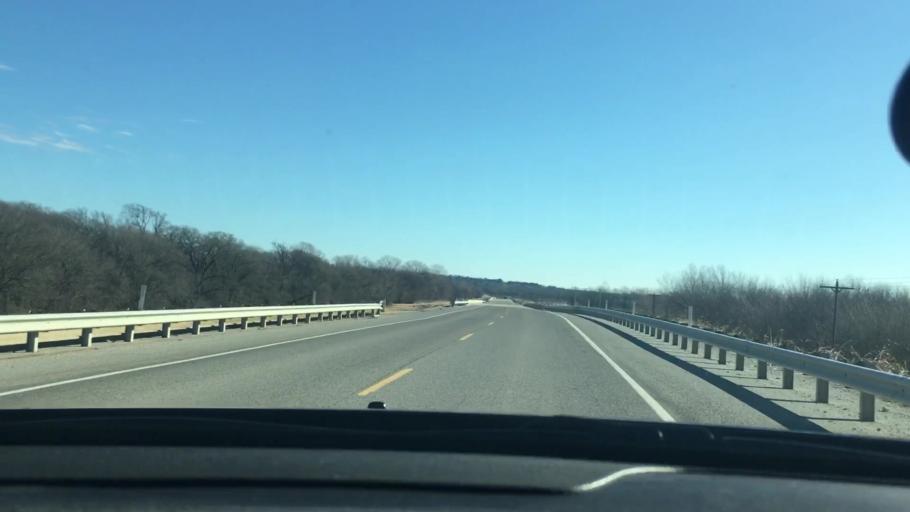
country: US
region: Oklahoma
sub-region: Love County
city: Marietta
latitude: 33.9402
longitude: -97.3051
